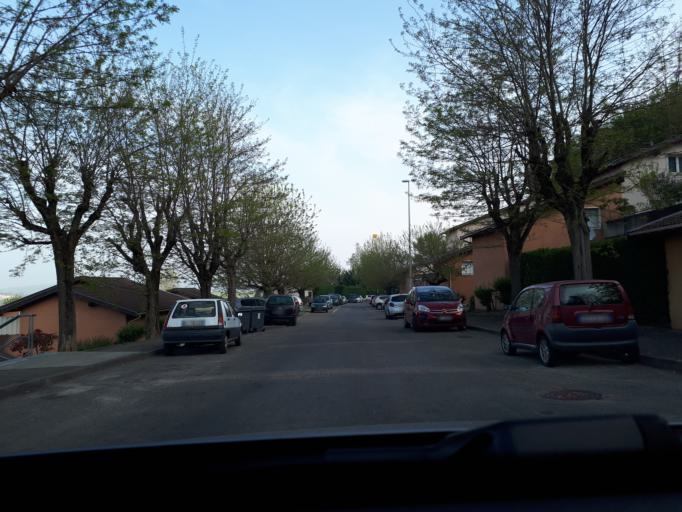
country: FR
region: Rhone-Alpes
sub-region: Departement de l'Isere
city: Bourgoin-Jallieu
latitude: 45.6045
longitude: 5.2742
